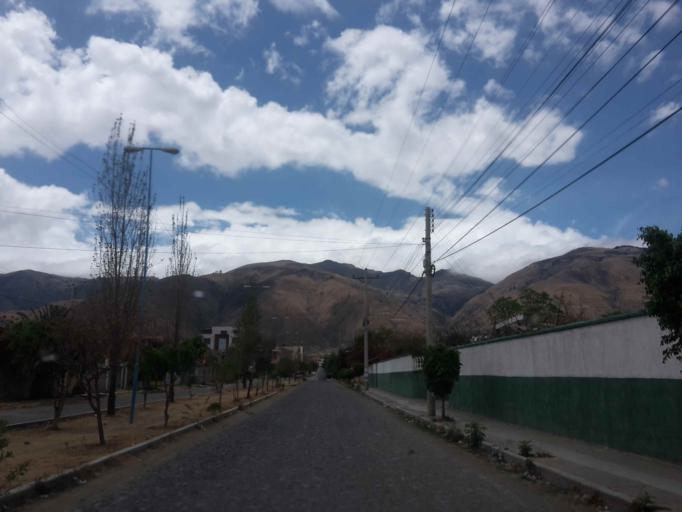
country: BO
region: Cochabamba
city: Cochabamba
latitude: -17.3473
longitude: -66.1973
